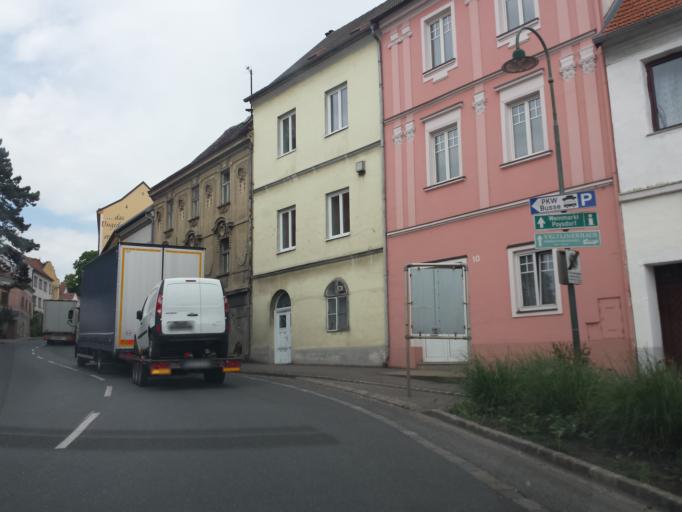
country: AT
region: Lower Austria
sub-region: Politischer Bezirk Mistelbach
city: Poysdorf
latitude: 48.6696
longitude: 16.6300
